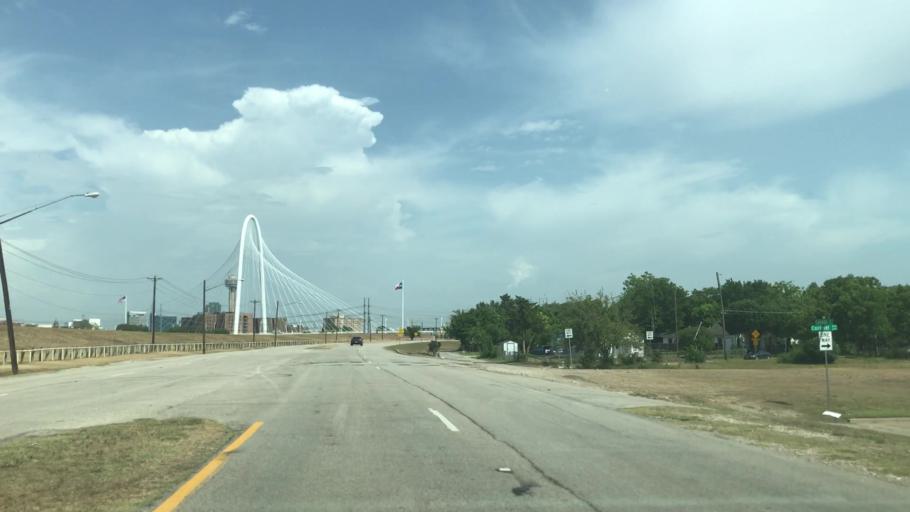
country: US
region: Texas
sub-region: Dallas County
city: Dallas
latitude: 32.7835
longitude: -96.8309
